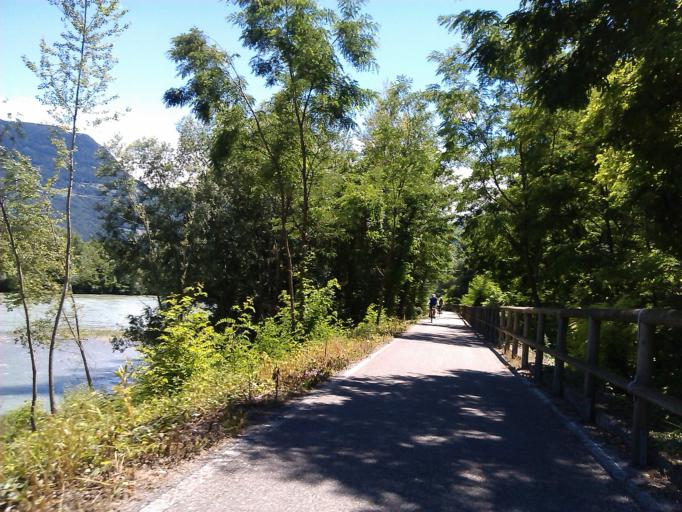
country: IT
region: Trentino-Alto Adige
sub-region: Bolzano
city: Cornaiano
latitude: 46.4524
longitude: 11.3048
